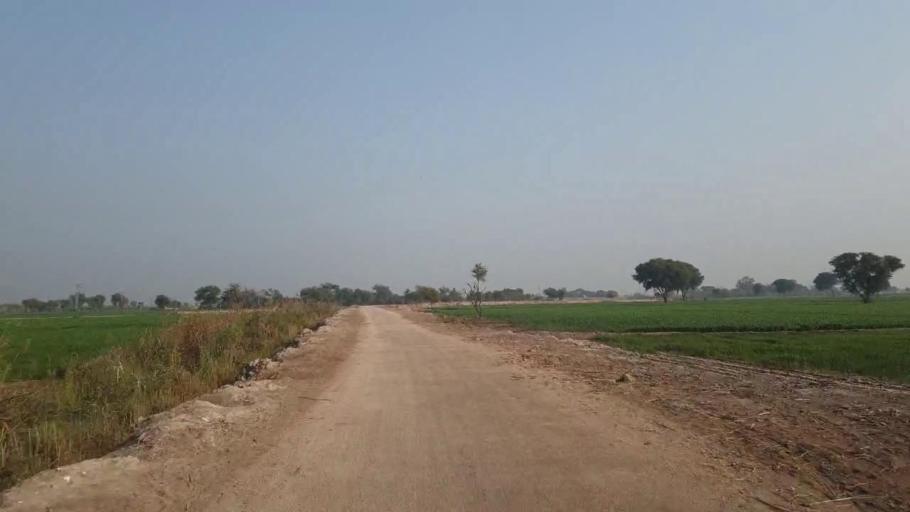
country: PK
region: Sindh
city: Shahdadpur
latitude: 25.9592
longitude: 68.5275
